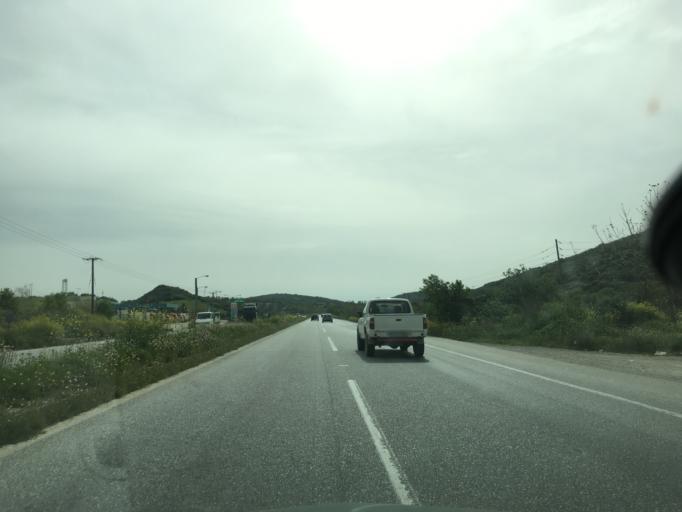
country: GR
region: Thessaly
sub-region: Nomos Magnisias
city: Velestino
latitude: 39.3830
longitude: 22.8222
